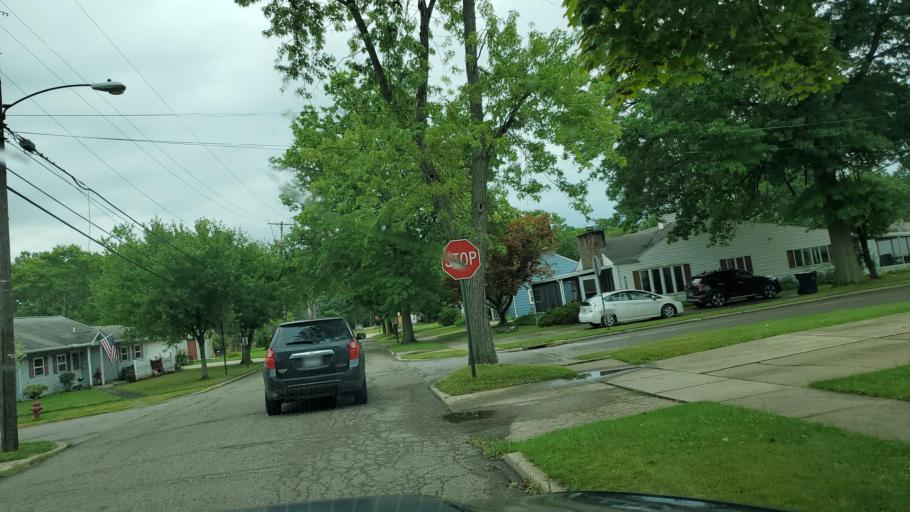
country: US
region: Ohio
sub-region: Trumbull County
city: McDonald
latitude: 41.1601
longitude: -80.7257
